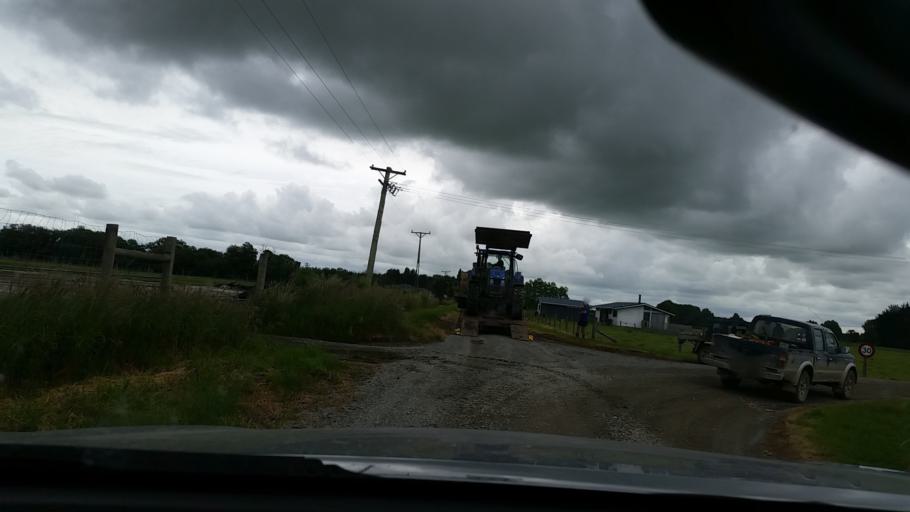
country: NZ
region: Southland
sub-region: Southland District
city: Winton
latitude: -46.0849
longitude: 168.3267
